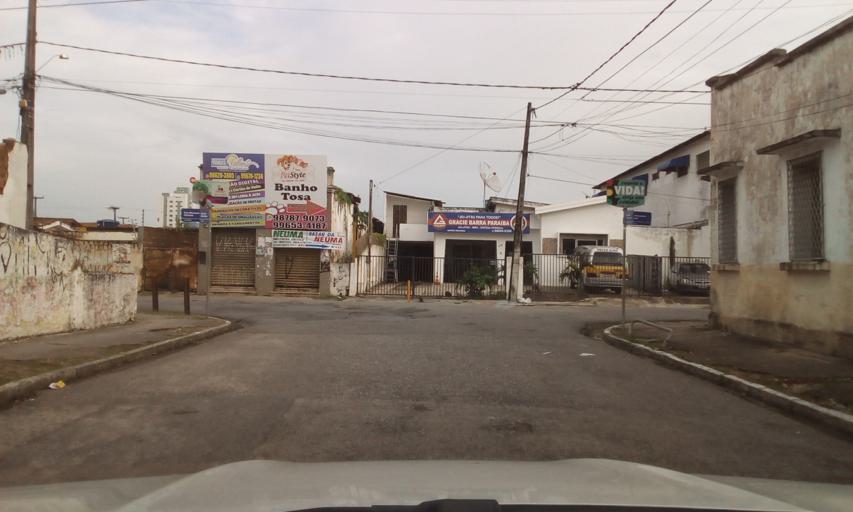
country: BR
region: Paraiba
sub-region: Joao Pessoa
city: Joao Pessoa
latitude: -7.1276
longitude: -34.8813
